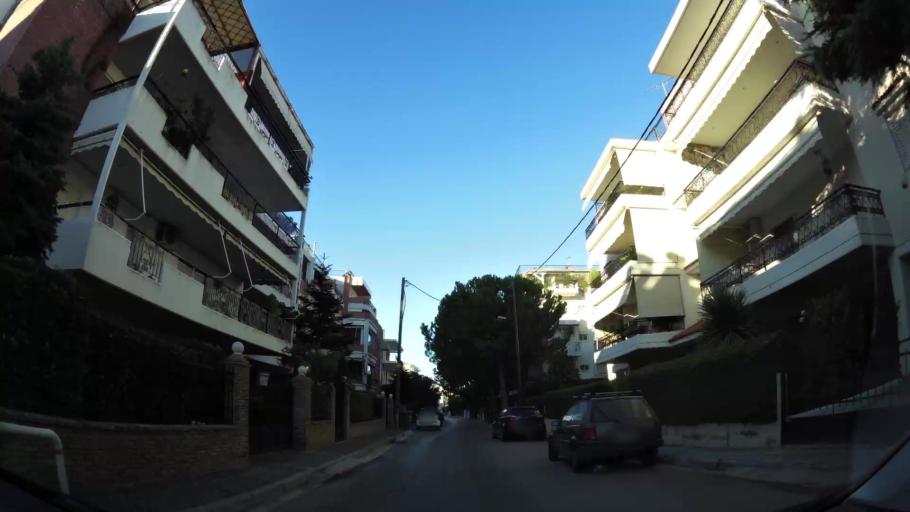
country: GR
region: Attica
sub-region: Nomarchia Anatolikis Attikis
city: Pallini
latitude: 38.0065
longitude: 23.8858
